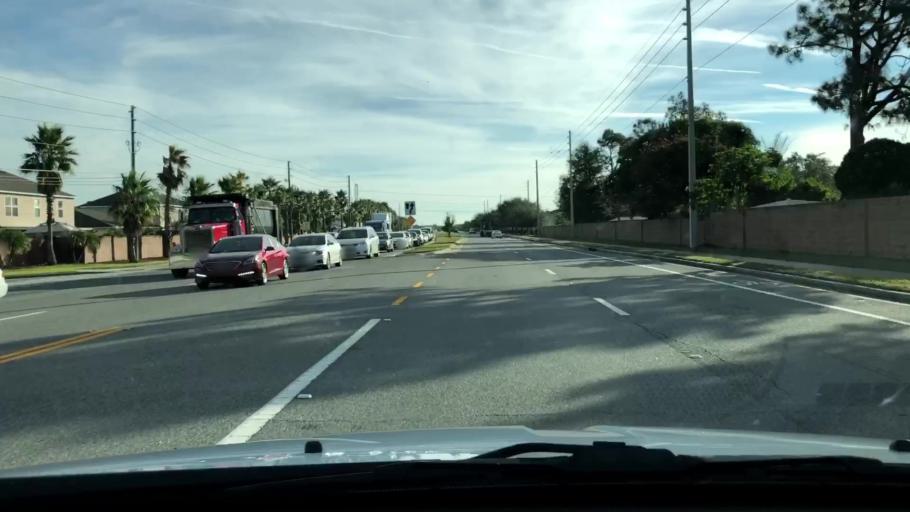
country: US
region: Florida
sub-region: Orange County
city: Meadow Woods
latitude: 28.3923
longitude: -81.3609
